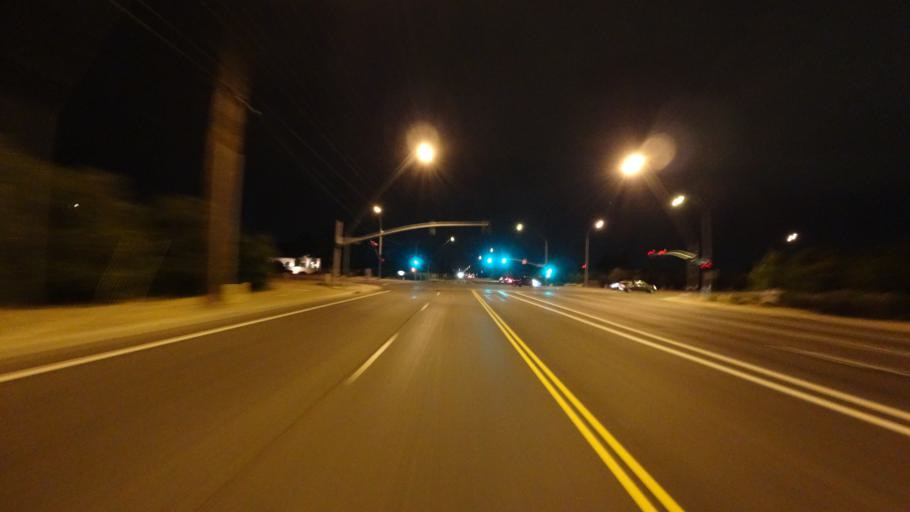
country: US
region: Arizona
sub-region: Maricopa County
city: Mesa
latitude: 33.4523
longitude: -111.7533
